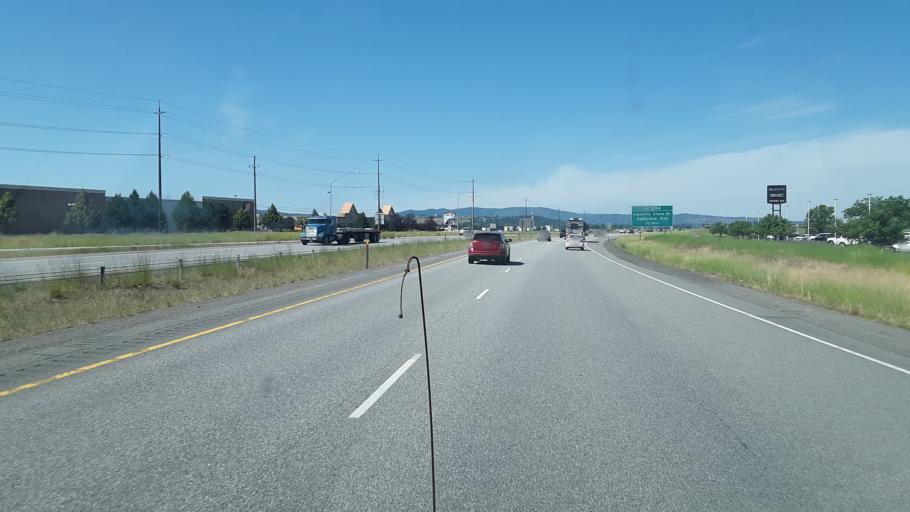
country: US
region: Washington
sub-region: Spokane County
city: Liberty Lake
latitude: 47.6704
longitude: -117.1144
